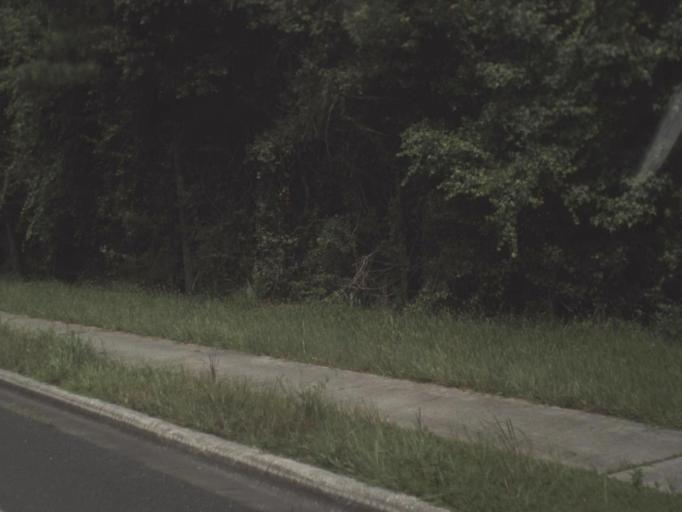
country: US
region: Florida
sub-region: Hernando County
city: South Brooksville
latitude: 28.5233
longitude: -82.4131
